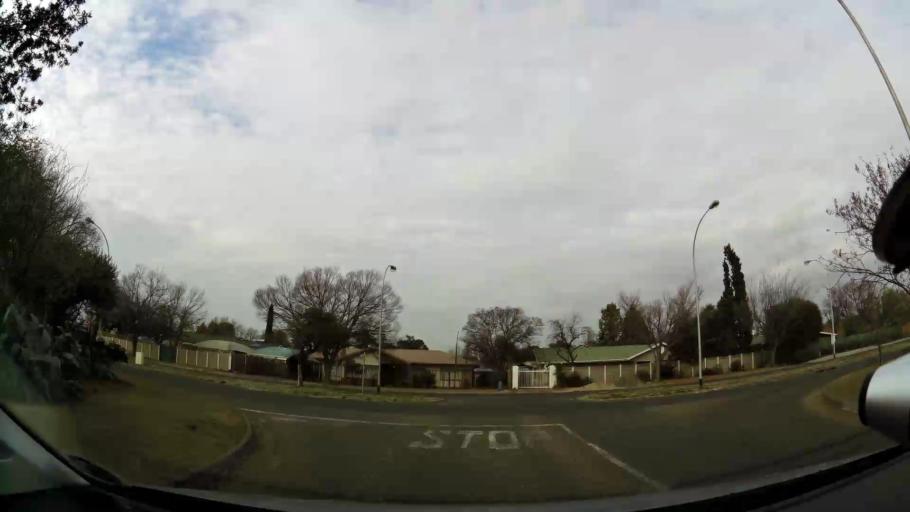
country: ZA
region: Orange Free State
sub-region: Mangaung Metropolitan Municipality
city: Bloemfontein
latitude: -29.1231
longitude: 26.1871
